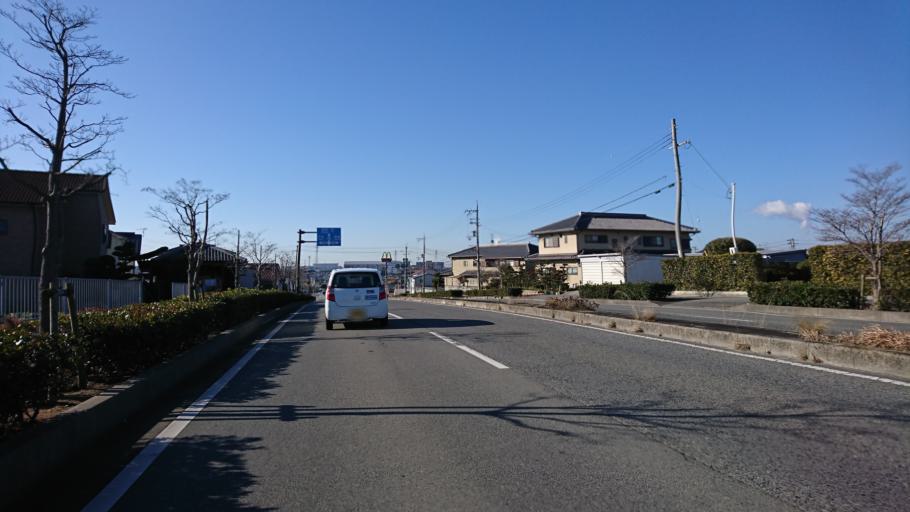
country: JP
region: Hyogo
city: Kakogawacho-honmachi
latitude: 34.7958
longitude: 134.8265
